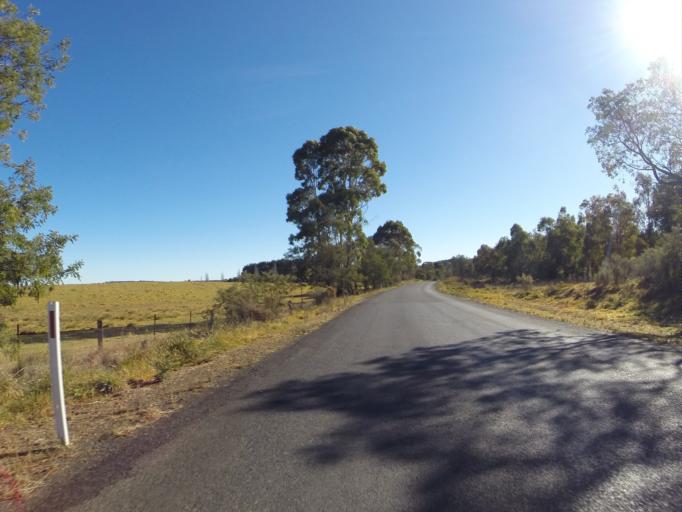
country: AU
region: New South Wales
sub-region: Oberon
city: Oberon
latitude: -33.6685
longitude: 149.8573
